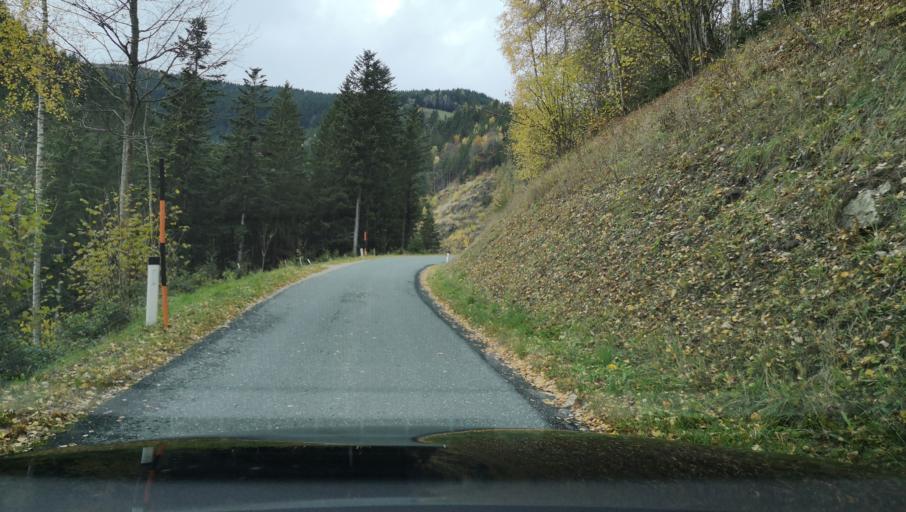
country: AT
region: Styria
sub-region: Politischer Bezirk Weiz
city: Birkfeld
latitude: 47.3661
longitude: 15.6326
